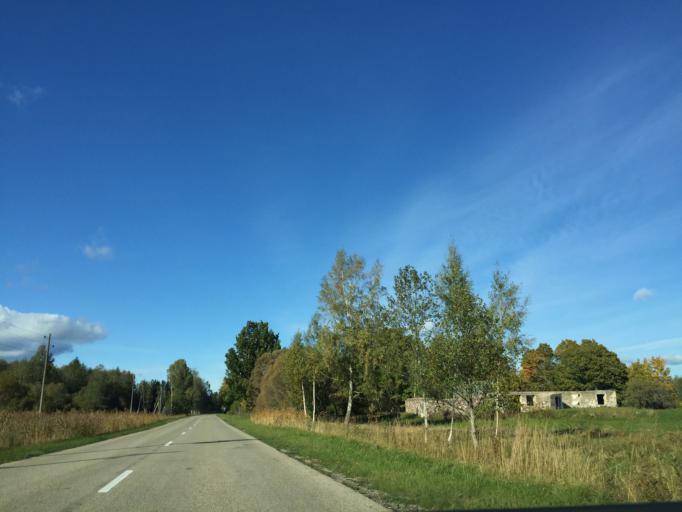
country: LV
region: Rojas
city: Roja
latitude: 57.4310
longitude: 22.9121
